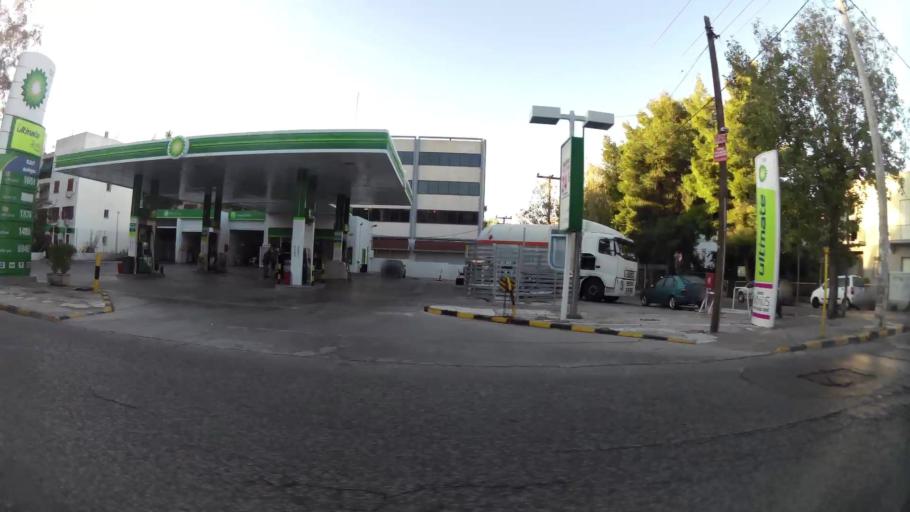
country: GR
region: Attica
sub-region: Nomarchia Athinas
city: Marousi
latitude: 38.0490
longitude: 23.8010
